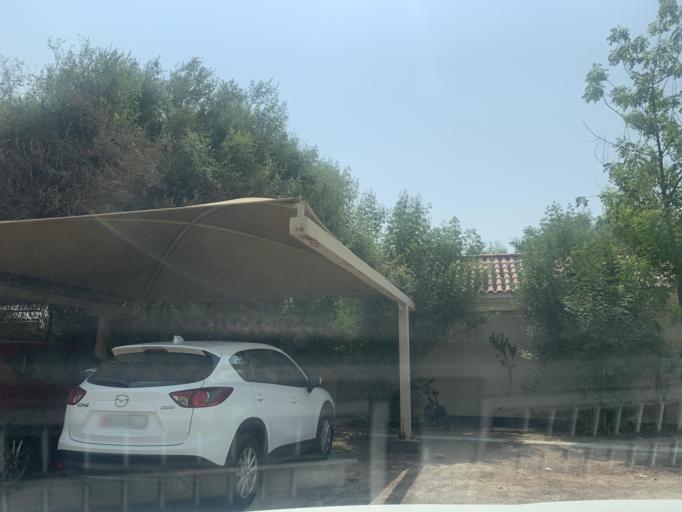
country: BH
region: Central Governorate
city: Madinat Hamad
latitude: 26.1598
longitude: 50.4540
